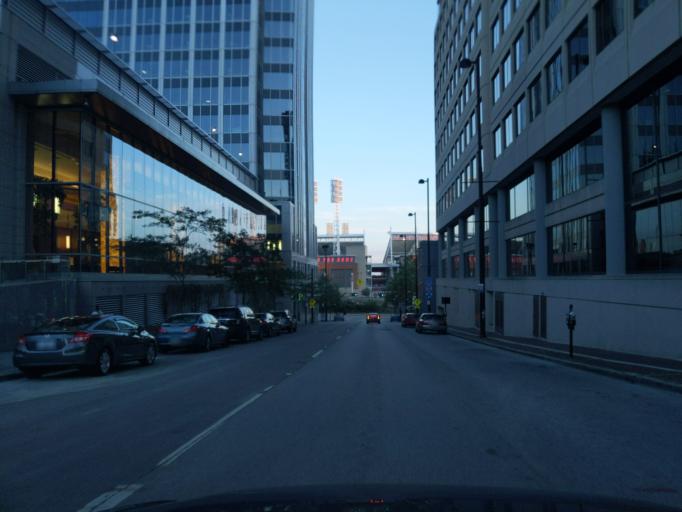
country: US
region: Kentucky
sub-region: Campbell County
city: Newport
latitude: 39.1006
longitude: -84.5079
